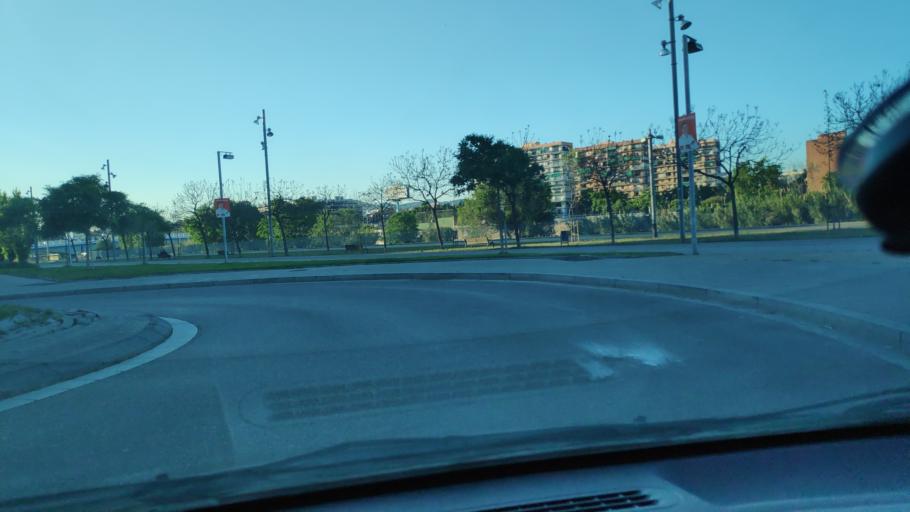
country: ES
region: Catalonia
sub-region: Provincia de Barcelona
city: Sant Adria de Besos
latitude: 41.4246
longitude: 2.2207
